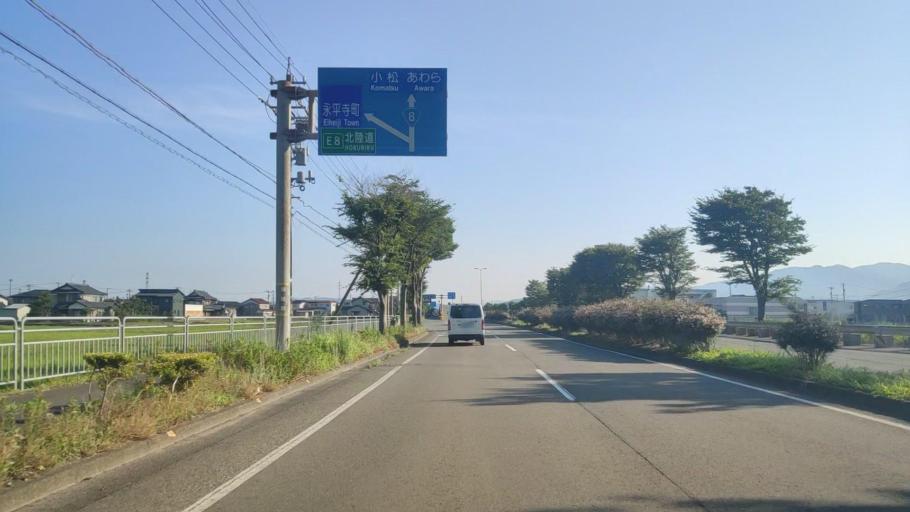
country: JP
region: Fukui
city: Maruoka
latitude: 36.1389
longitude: 136.2633
